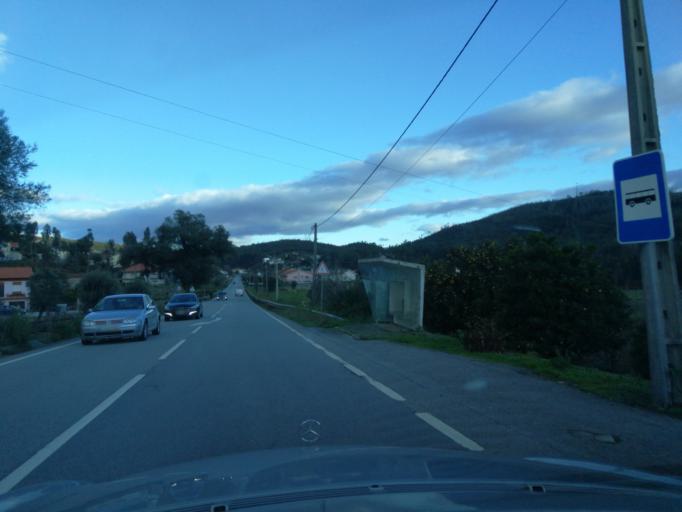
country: PT
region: Braga
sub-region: Barcelos
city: Vila Frescainha
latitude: 41.5726
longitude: -8.6965
